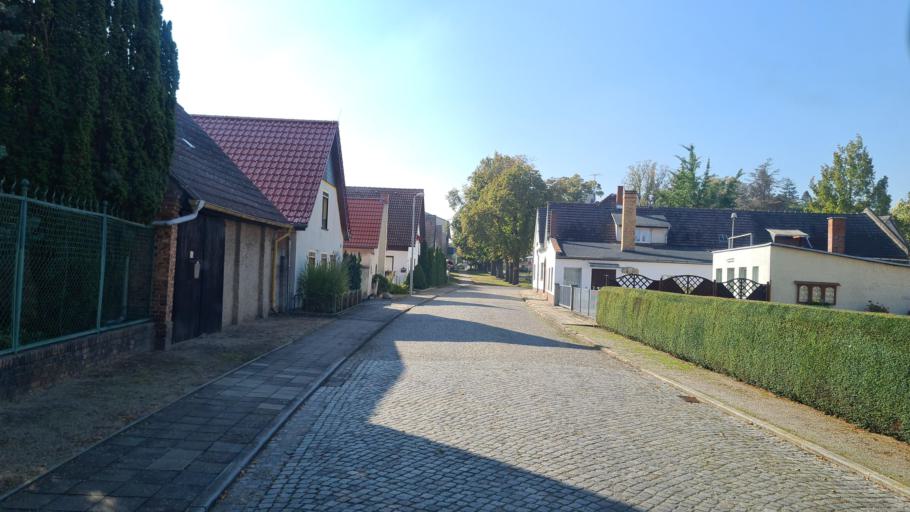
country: DE
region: Brandenburg
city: Luckau
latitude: 51.8500
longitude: 13.7057
